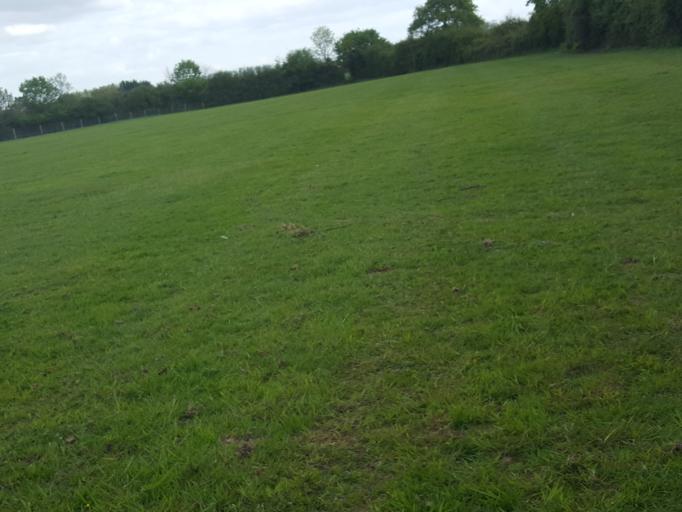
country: GB
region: England
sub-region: Essex
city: Frinton-on-Sea
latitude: 51.8400
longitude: 1.2078
